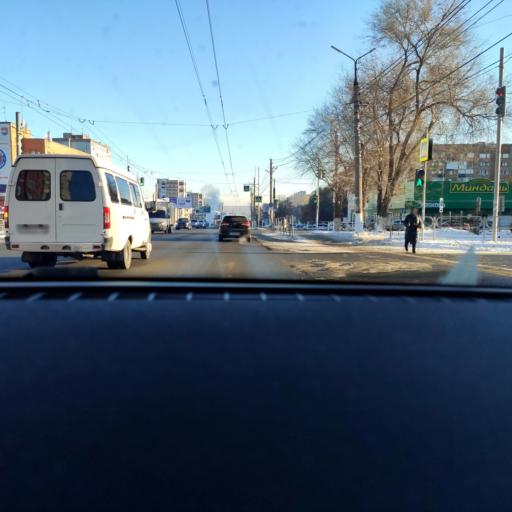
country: RU
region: Samara
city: Novokuybyshevsk
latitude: 53.0936
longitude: 49.9780
